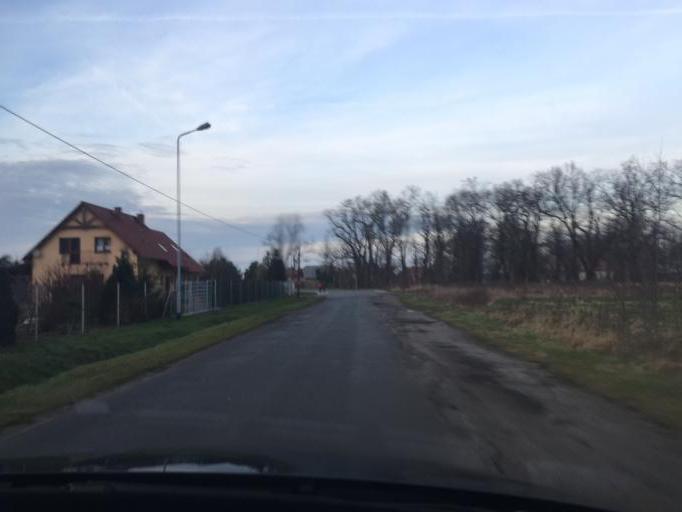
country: PL
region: Lubusz
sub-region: Powiat zielonogorski
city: Ochla
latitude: 51.8095
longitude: 15.4906
